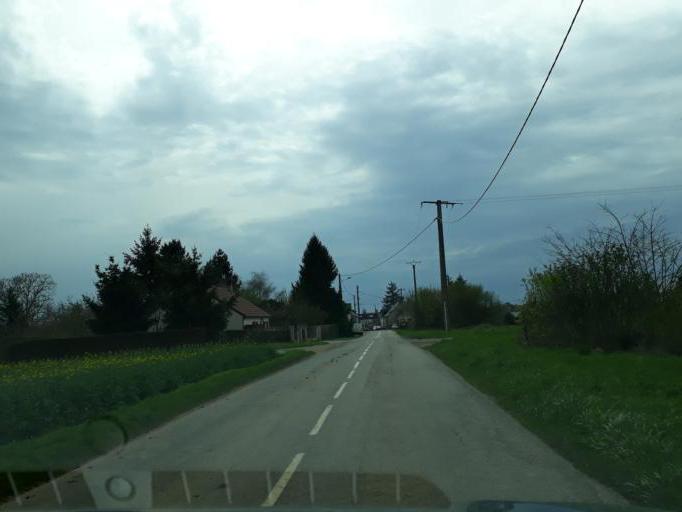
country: FR
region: Centre
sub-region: Departement du Loiret
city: Epieds-en-Beauce
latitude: 47.9312
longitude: 1.5789
